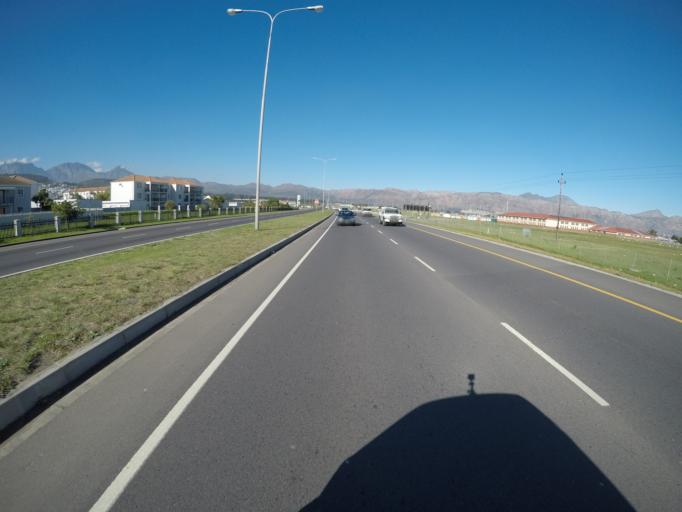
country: ZA
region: Western Cape
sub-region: Overberg District Municipality
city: Grabouw
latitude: -34.1062
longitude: 18.8577
